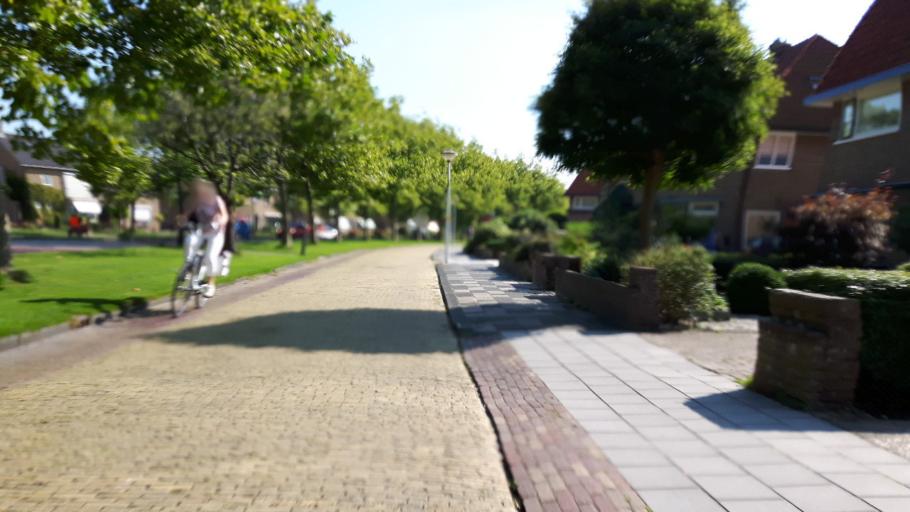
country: NL
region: Friesland
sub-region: Gemeente Franekeradeel
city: Franeker
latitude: 53.1921
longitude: 5.5413
